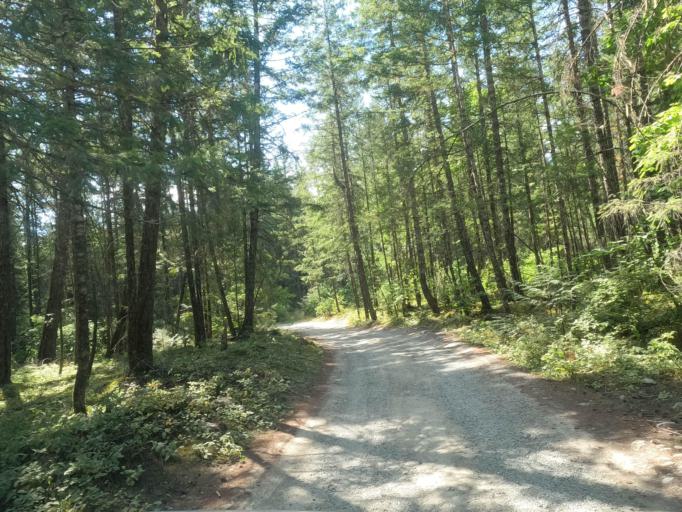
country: CA
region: British Columbia
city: Pemberton
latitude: 50.3524
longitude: -122.7315
